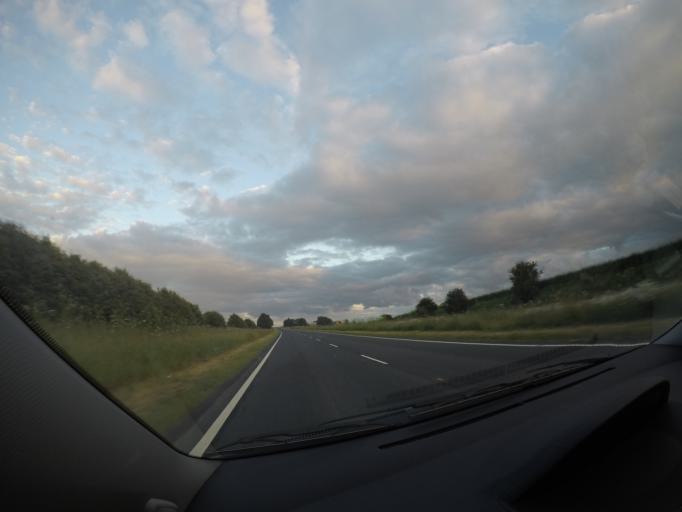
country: GB
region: England
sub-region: North Yorkshire
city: Bedale
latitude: 54.2465
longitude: -1.5053
